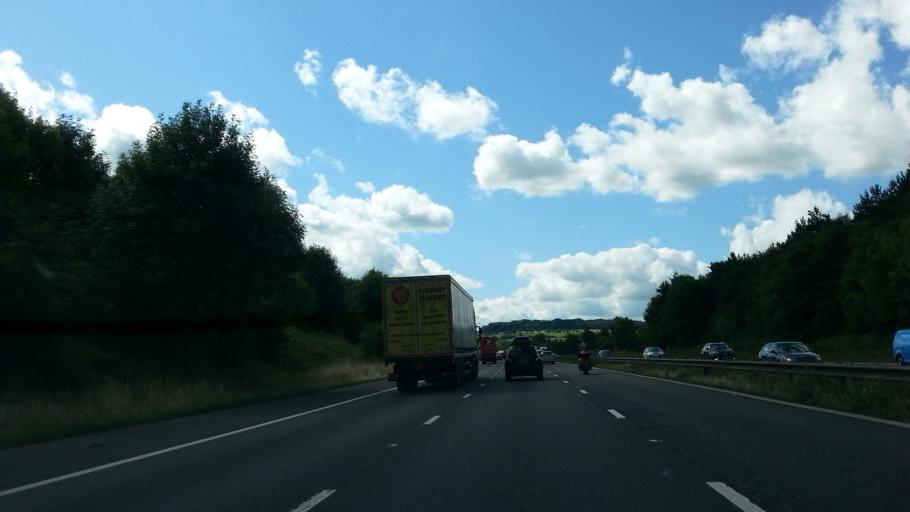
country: GB
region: England
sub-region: Leicestershire
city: Shepshed
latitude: 52.7381
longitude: -1.2806
